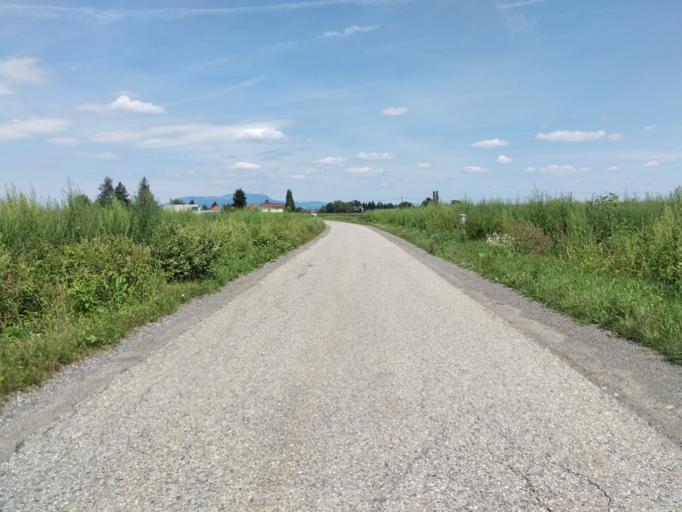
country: AT
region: Styria
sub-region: Politischer Bezirk Graz-Umgebung
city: Kalsdorf bei Graz
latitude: 46.9765
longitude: 15.4484
